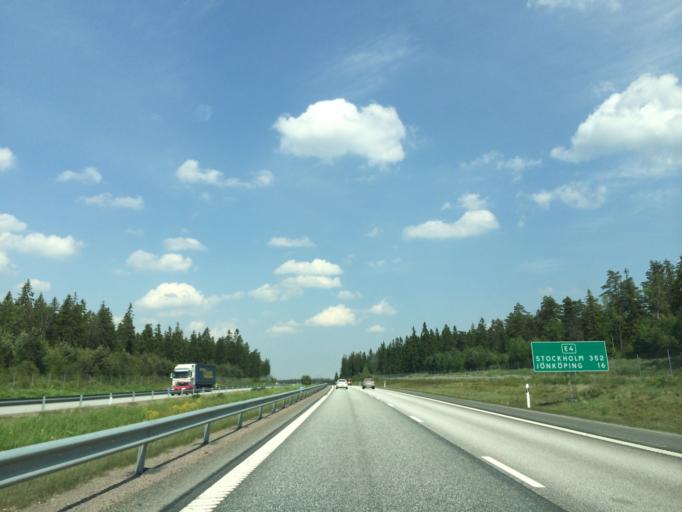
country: SE
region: Joenkoeping
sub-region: Jonkopings Kommun
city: Odensjo
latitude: 57.6343
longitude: 14.1879
